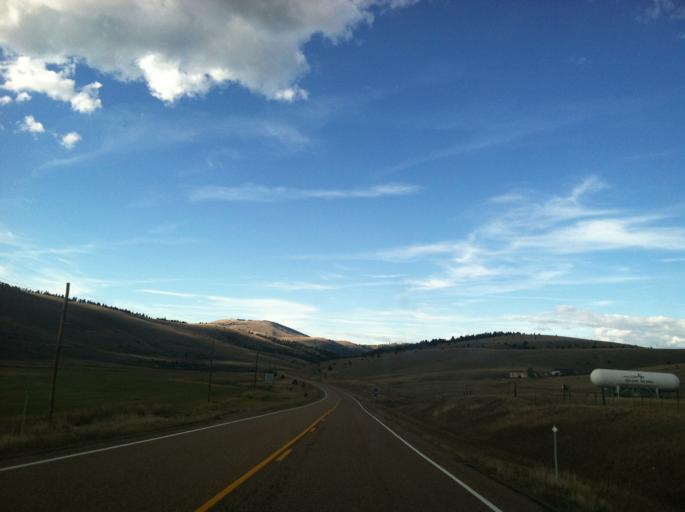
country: US
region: Montana
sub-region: Granite County
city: Philipsburg
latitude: 46.3743
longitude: -113.3131
